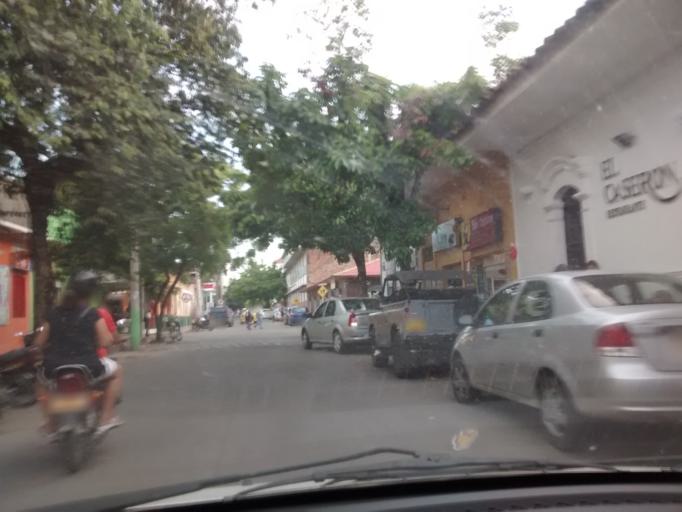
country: CO
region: Cundinamarca
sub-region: Girardot
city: Girardot City
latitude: 4.2986
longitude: -74.8066
